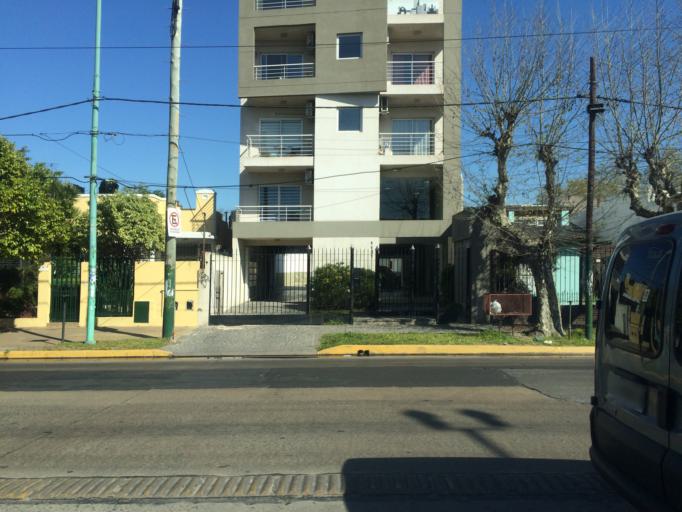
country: AR
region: Buenos Aires
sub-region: Partido de Lomas de Zamora
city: Lomas de Zamora
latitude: -34.7498
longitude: -58.3945
